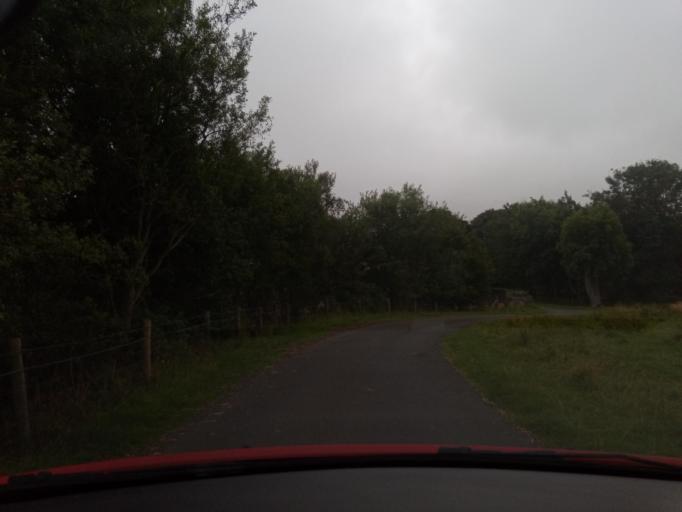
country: GB
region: England
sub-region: Northumberland
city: Otterburn
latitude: 55.2788
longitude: -2.0950
